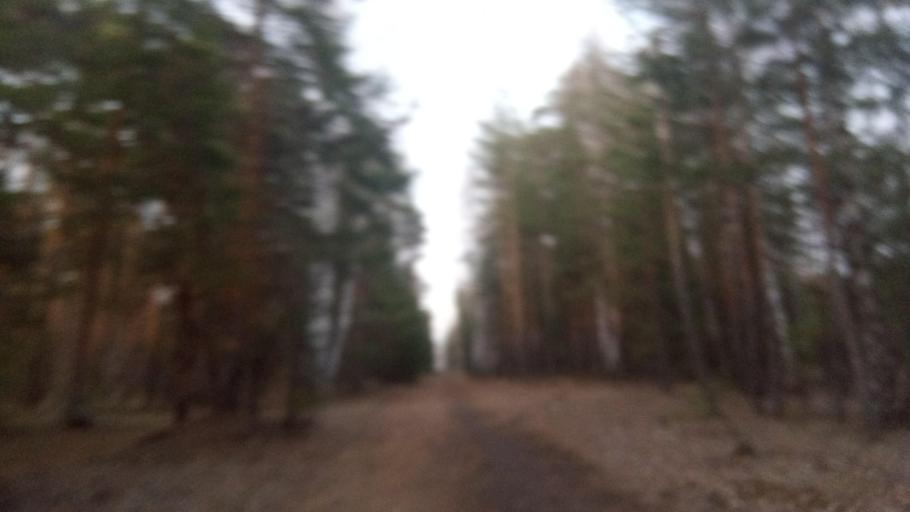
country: RU
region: Chelyabinsk
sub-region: Gorod Chelyabinsk
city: Chelyabinsk
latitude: 55.1552
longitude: 61.3473
